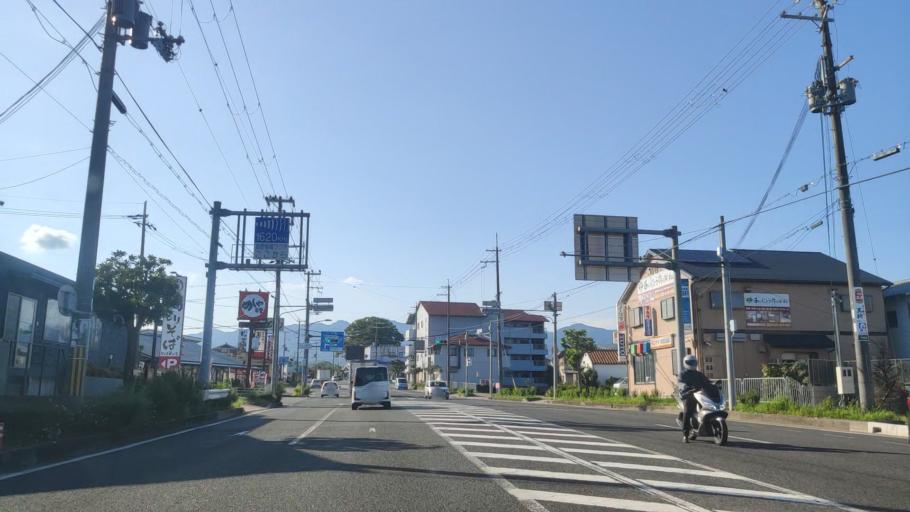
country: JP
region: Hyogo
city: Sandacho
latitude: 34.8345
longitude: 135.2401
